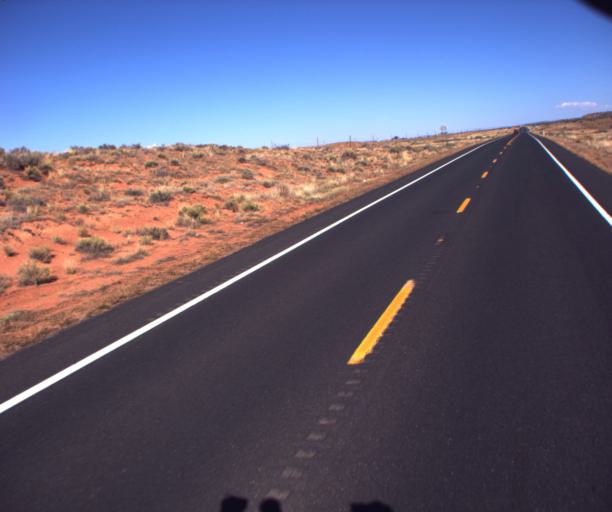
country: US
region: Arizona
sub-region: Coconino County
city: Kaibito
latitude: 36.3954
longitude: -110.8695
